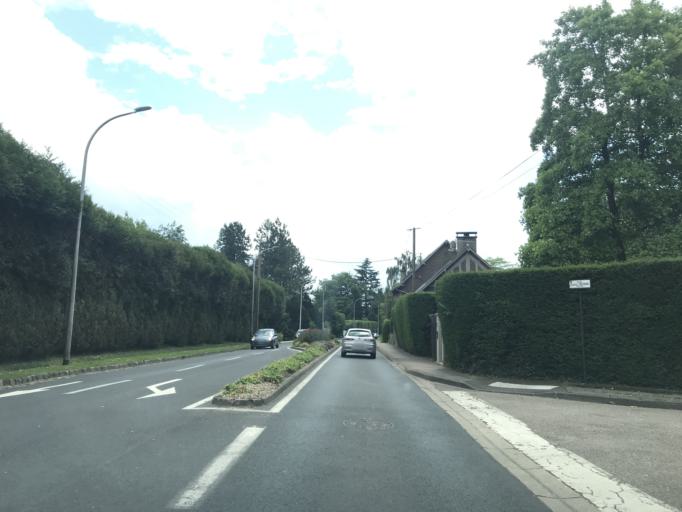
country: FR
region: Haute-Normandie
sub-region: Departement de la Seine-Maritime
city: Mont-Saint-Aignan
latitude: 49.4677
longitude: 1.0896
